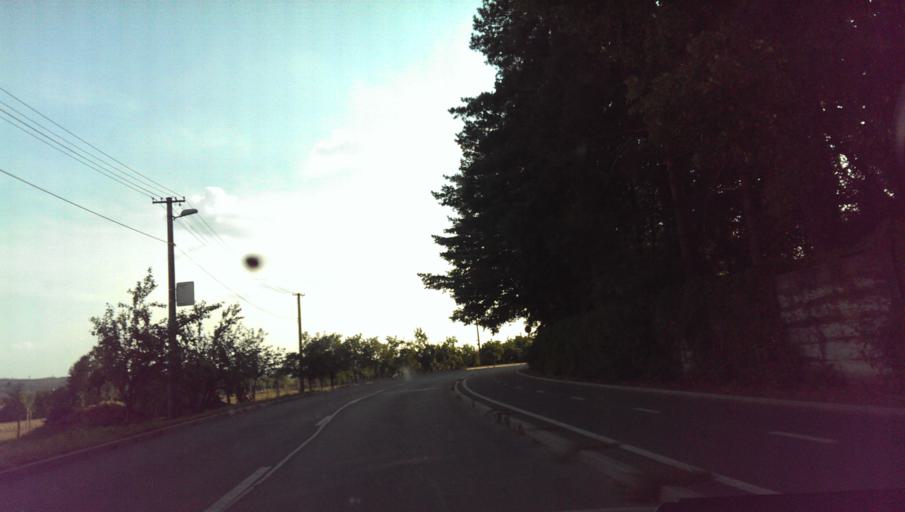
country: CZ
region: Zlin
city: Lukov
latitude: 49.2729
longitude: 17.7187
